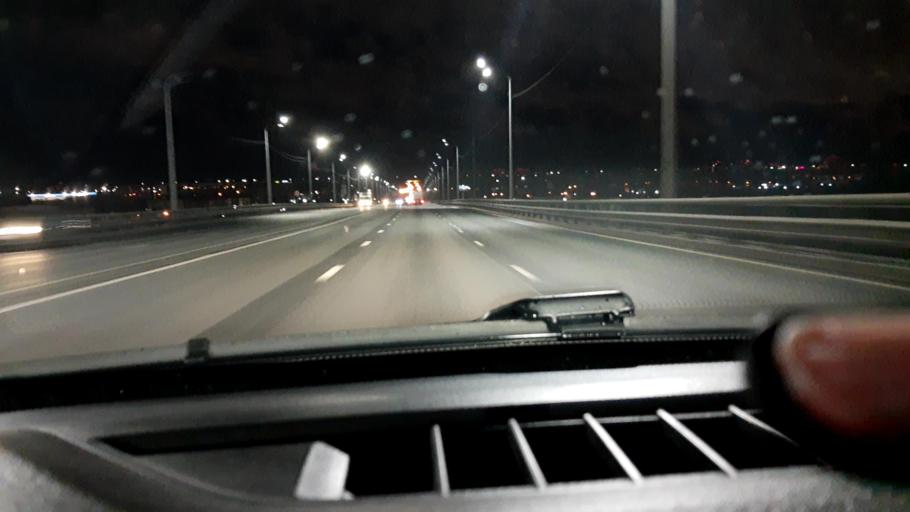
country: RU
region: Nizjnij Novgorod
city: Nizhniy Novgorod
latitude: 56.2491
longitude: 43.9506
